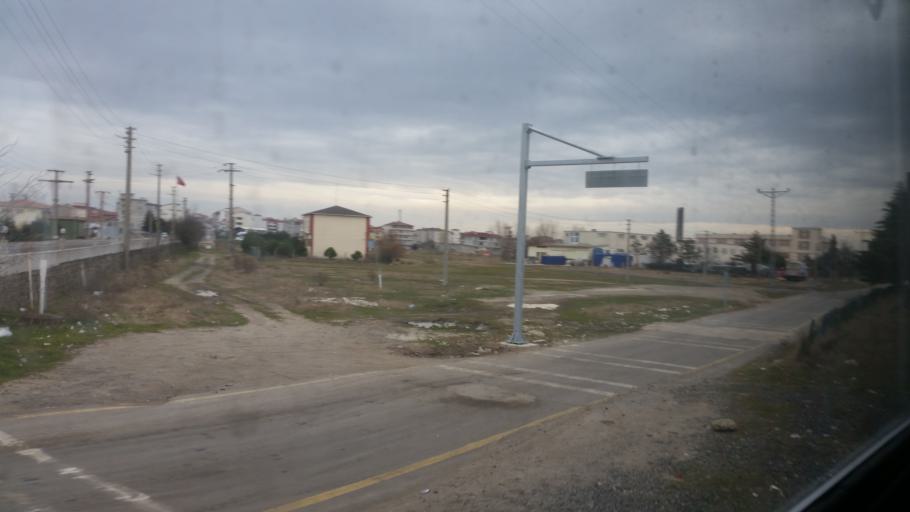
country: TR
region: Tekirdag
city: Velimese
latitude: 41.2439
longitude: 27.8836
